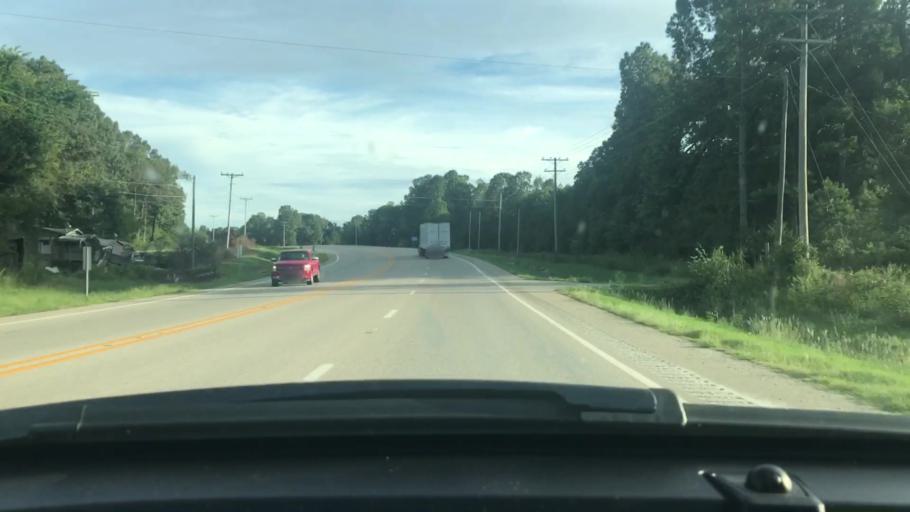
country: US
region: Arkansas
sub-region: Lawrence County
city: Hoxie
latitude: 36.1318
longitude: -91.1584
